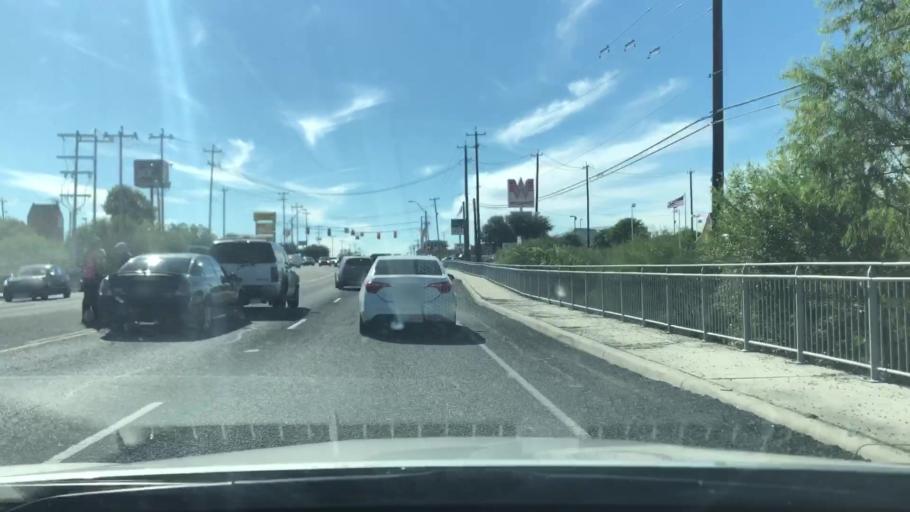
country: US
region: Texas
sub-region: Bexar County
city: Converse
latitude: 29.4924
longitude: -98.3330
